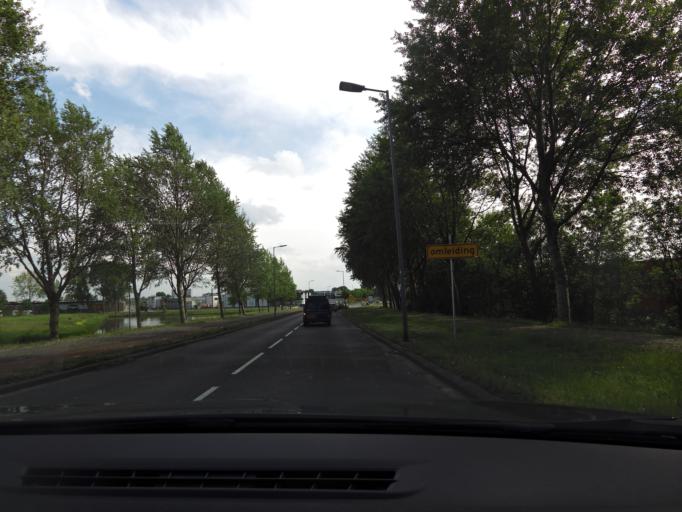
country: NL
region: South Holland
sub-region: Gemeente Schiedam
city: Schiedam
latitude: 51.9363
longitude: 4.4117
